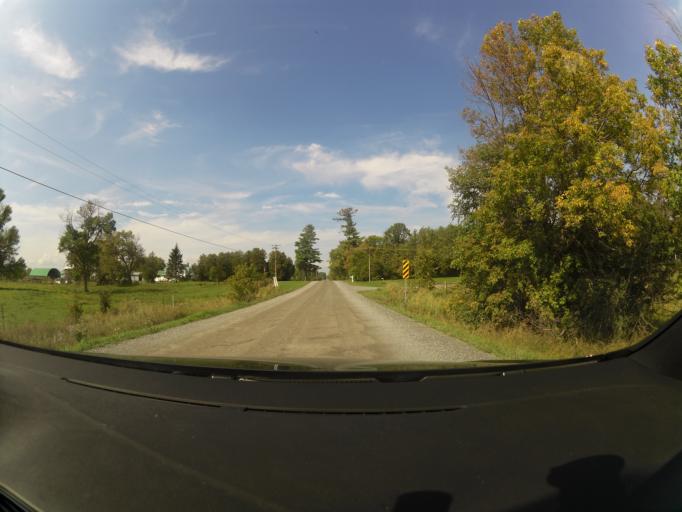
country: CA
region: Ontario
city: Carleton Place
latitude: 45.3284
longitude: -76.1780
